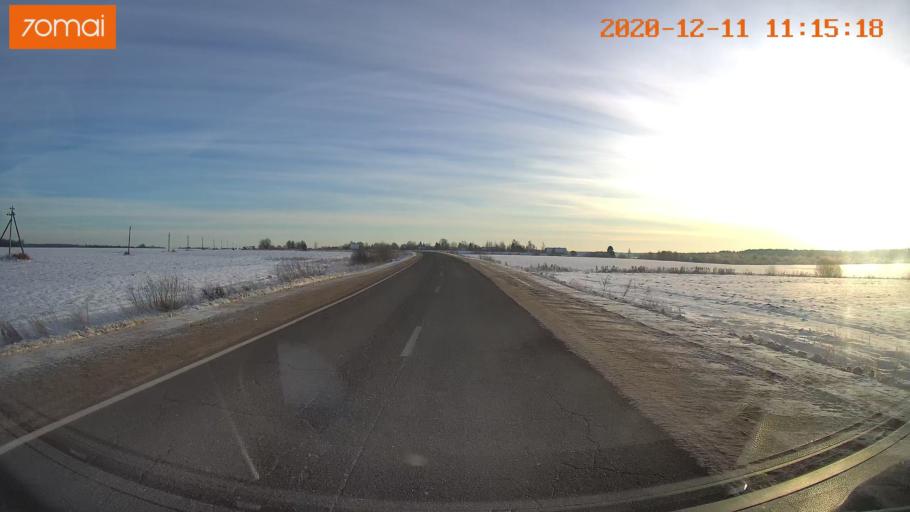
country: RU
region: Jaroslavl
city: Lyubim
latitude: 58.3185
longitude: 40.9302
